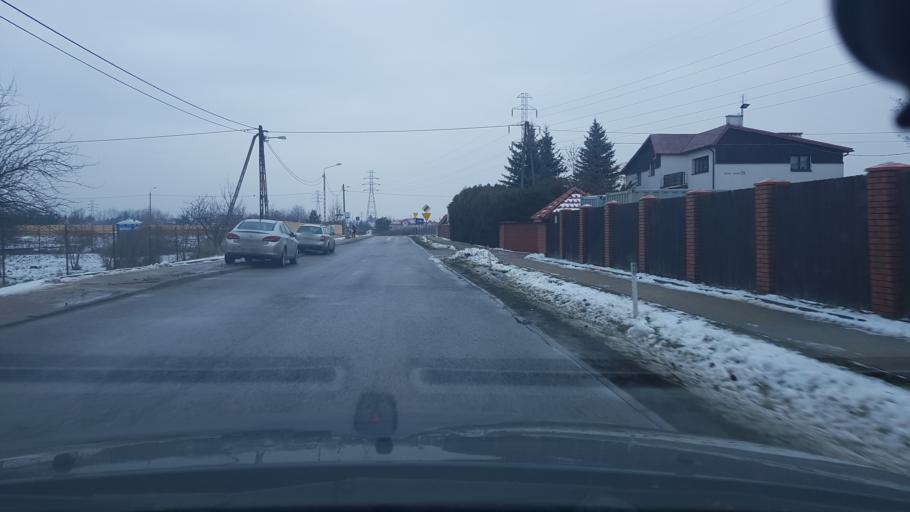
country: PL
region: Masovian Voivodeship
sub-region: Warszawa
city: Targowek
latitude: 52.3166
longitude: 21.0373
